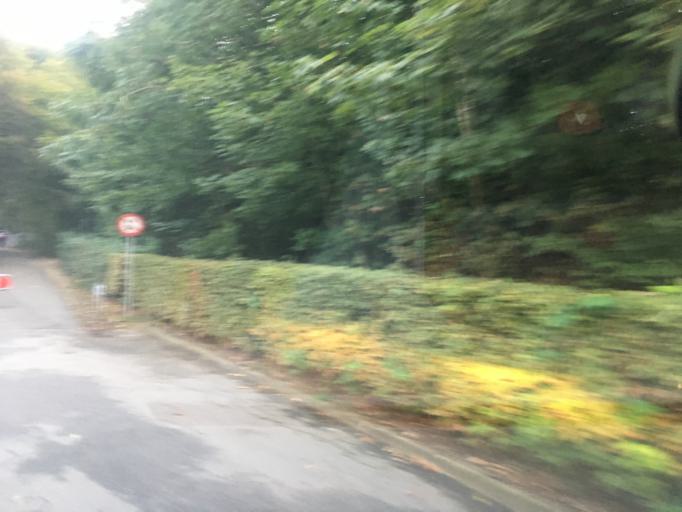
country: DK
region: South Denmark
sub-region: Tonder Kommune
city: Tonder
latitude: 54.9405
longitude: 8.8788
